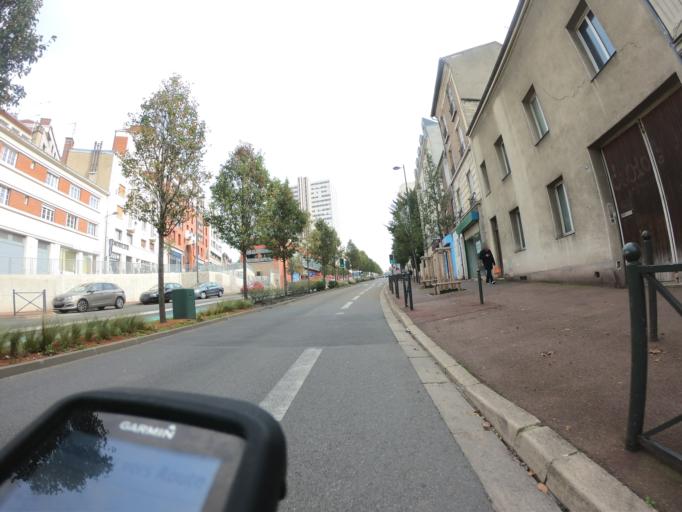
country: FR
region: Ile-de-France
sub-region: Departement des Hauts-de-Seine
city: Vanves
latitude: 48.8217
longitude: 2.2868
